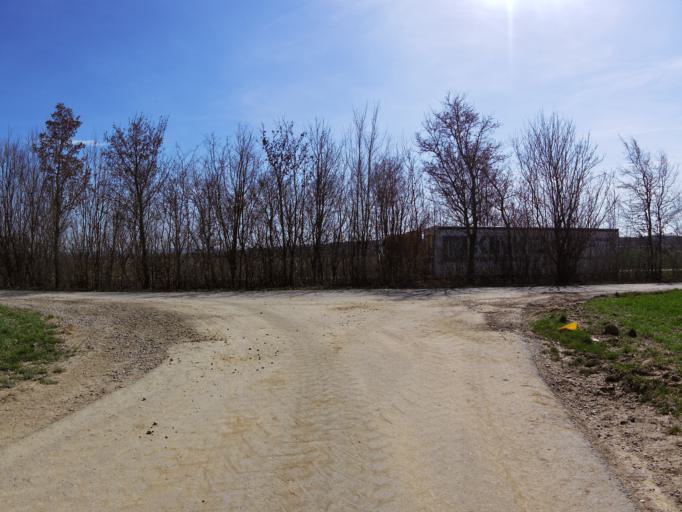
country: DE
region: Bavaria
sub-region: Regierungsbezirk Unterfranken
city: Biebelried
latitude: 49.7905
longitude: 10.1062
